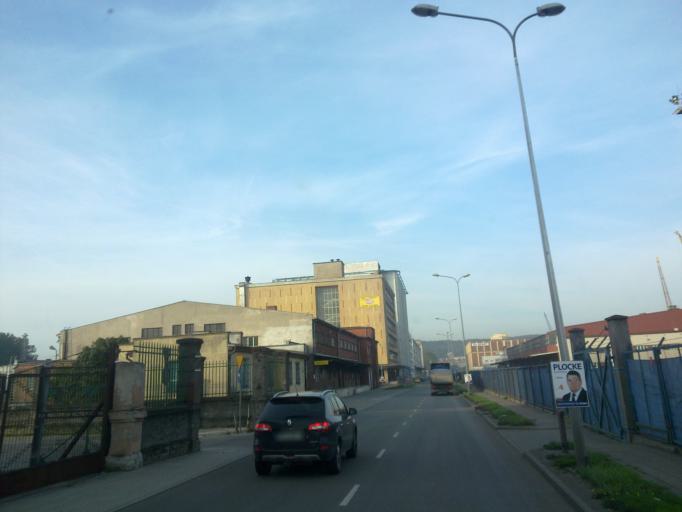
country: PL
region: Pomeranian Voivodeship
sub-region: Gdynia
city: Gdynia
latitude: 54.5300
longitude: 18.5375
